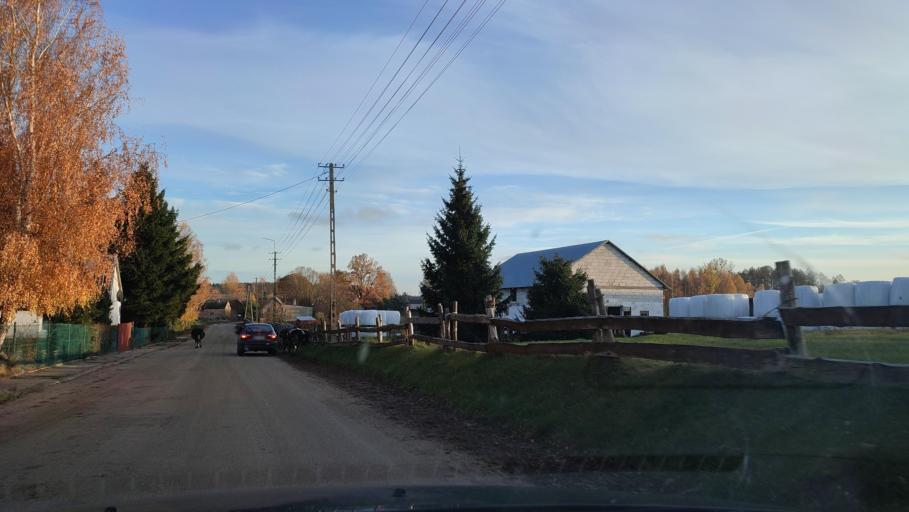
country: PL
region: Masovian Voivodeship
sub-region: Powiat mlawski
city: Dzierzgowo
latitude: 53.2787
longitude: 20.6461
